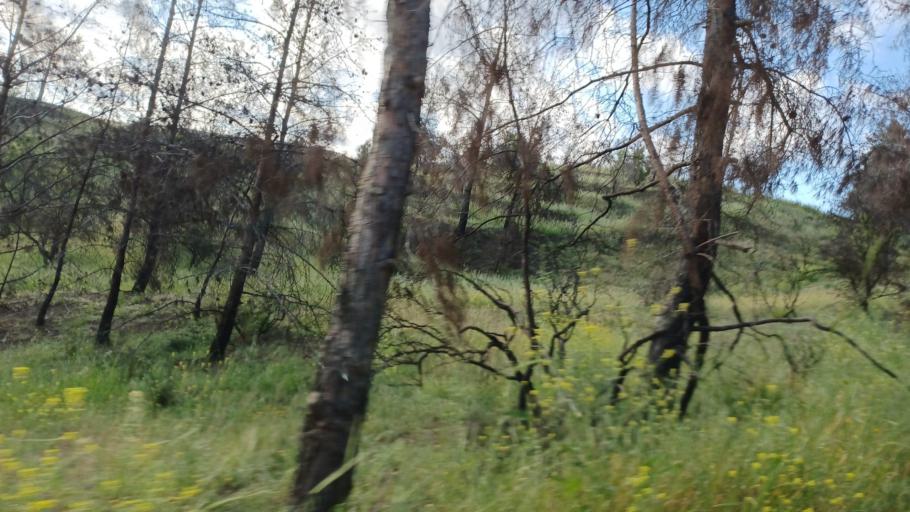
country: CY
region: Lefkosia
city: Peristerona
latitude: 35.0298
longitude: 33.0585
